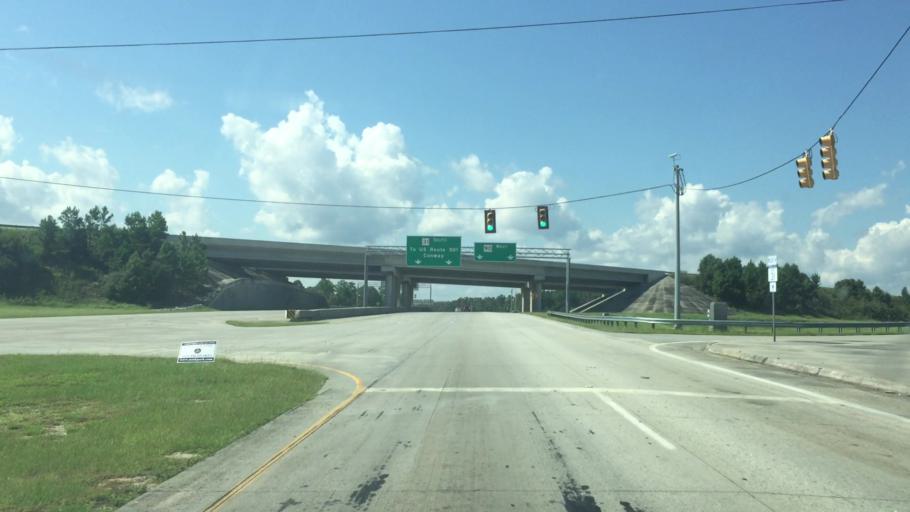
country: US
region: South Carolina
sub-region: Horry County
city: North Myrtle Beach
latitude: 33.8428
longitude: -78.7006
